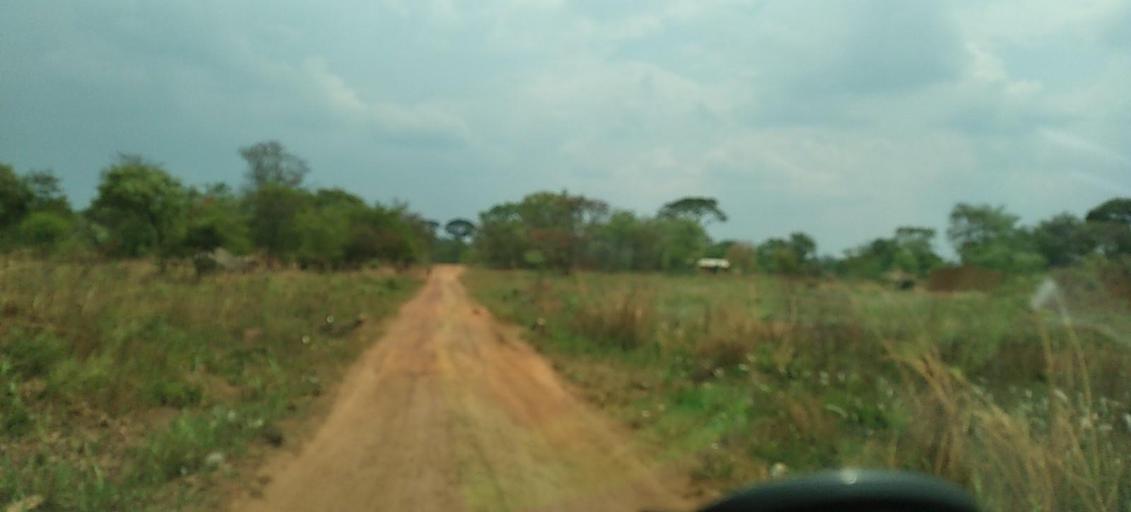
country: ZM
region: North-Western
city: Kansanshi
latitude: -11.9933
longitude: 26.2803
